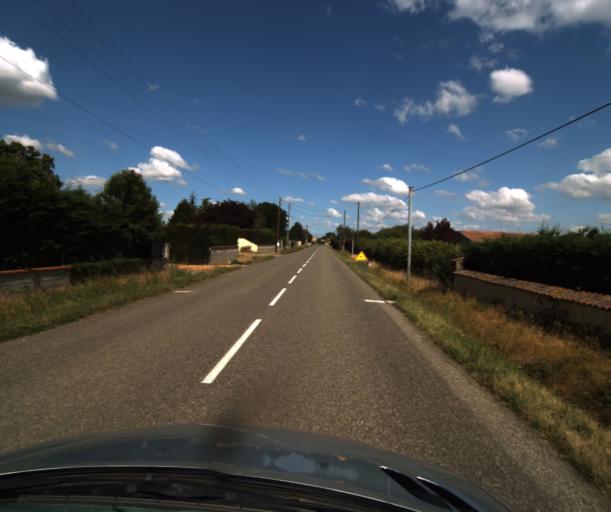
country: FR
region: Midi-Pyrenees
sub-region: Departement du Tarn-et-Garonne
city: Campsas
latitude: 43.9109
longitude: 1.2829
